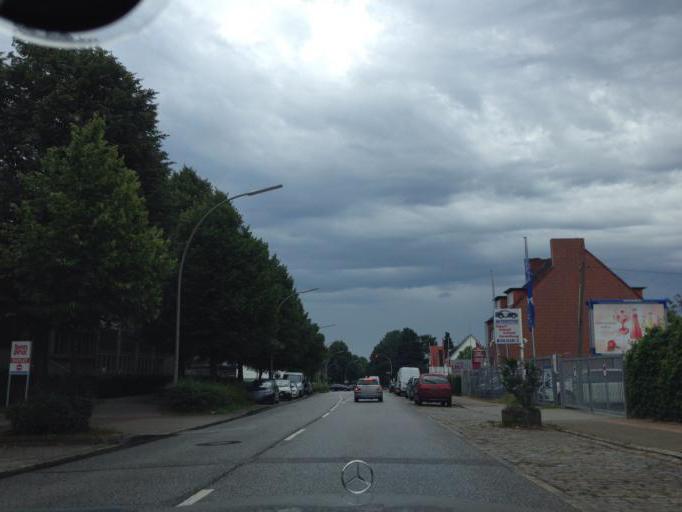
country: DE
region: Hamburg
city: Steilshoop
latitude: 53.5985
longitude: 10.0708
